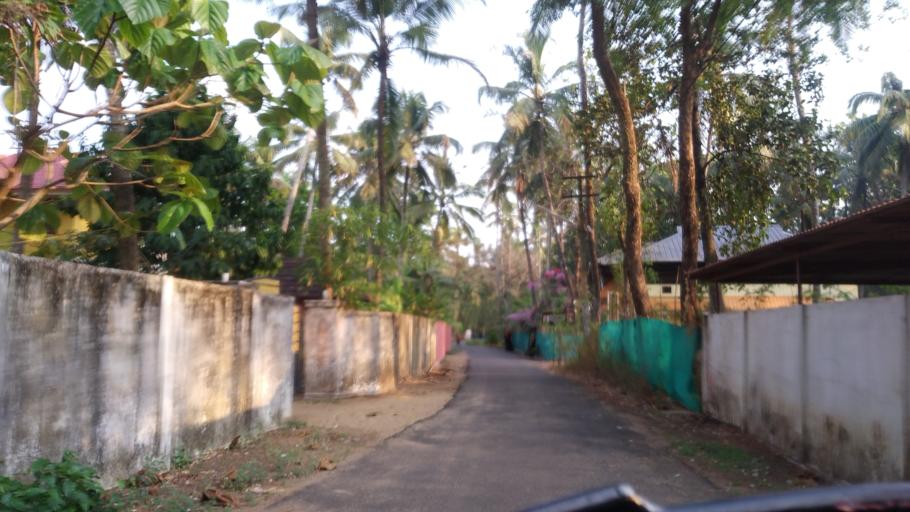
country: IN
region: Kerala
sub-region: Thrissur District
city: Thanniyam
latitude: 10.4106
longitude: 76.0888
